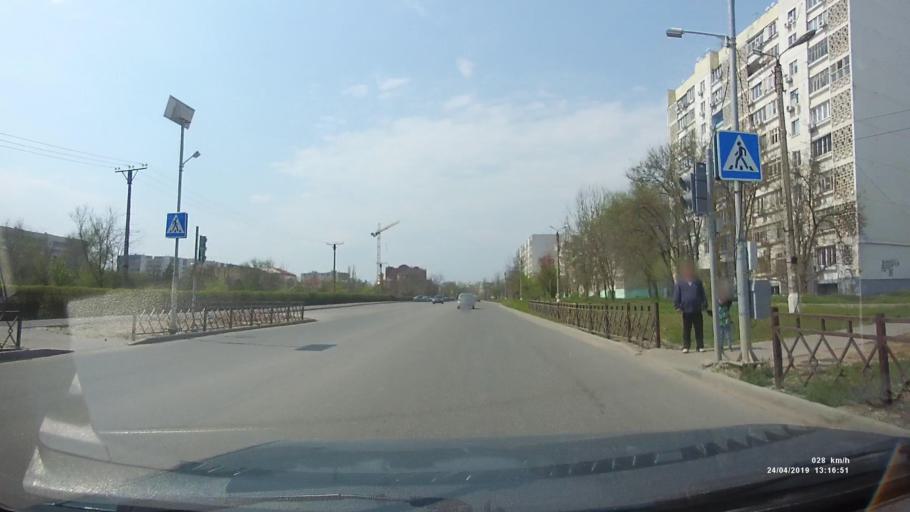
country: RU
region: Kalmykiya
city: Elista
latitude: 46.3047
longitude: 44.3033
